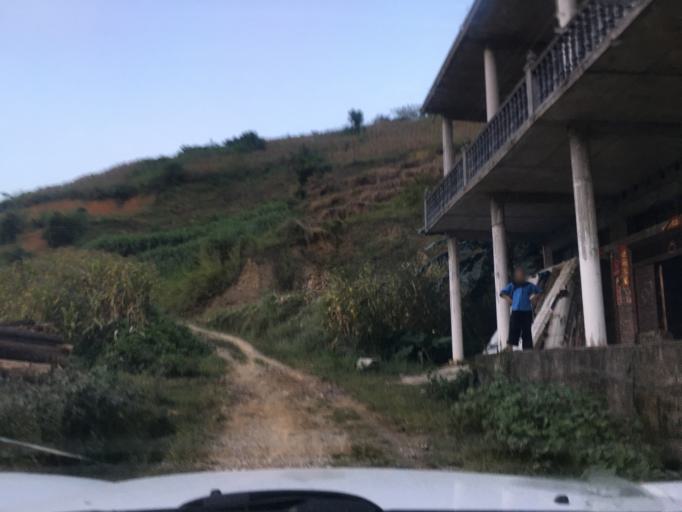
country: CN
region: Guangxi Zhuangzu Zizhiqu
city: Xinzhou
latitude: 25.3470
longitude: 105.7386
